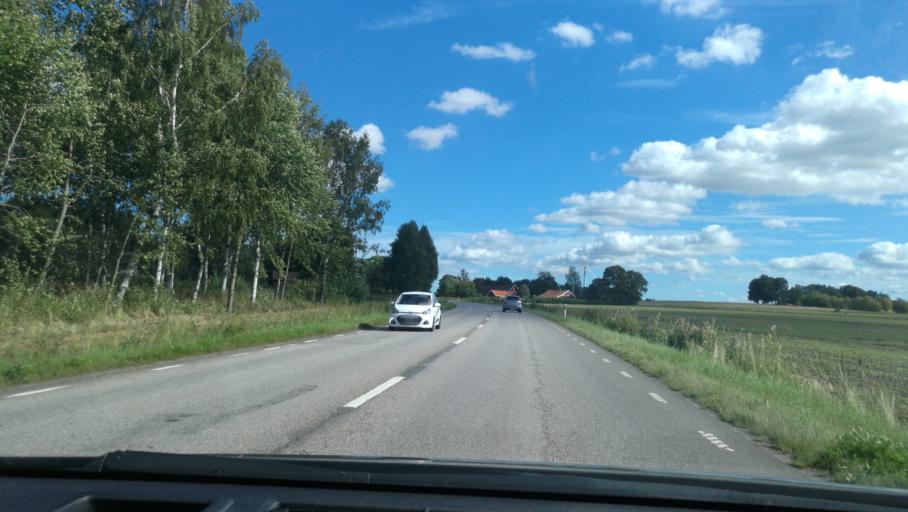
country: SE
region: Vaestra Goetaland
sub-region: Gotene Kommun
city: Kallby
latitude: 58.4911
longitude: 13.2848
